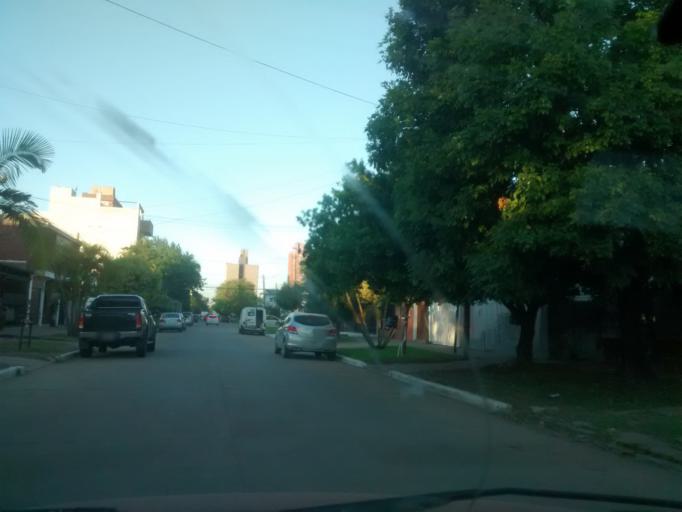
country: AR
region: Chaco
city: Resistencia
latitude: -27.4581
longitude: -58.9977
